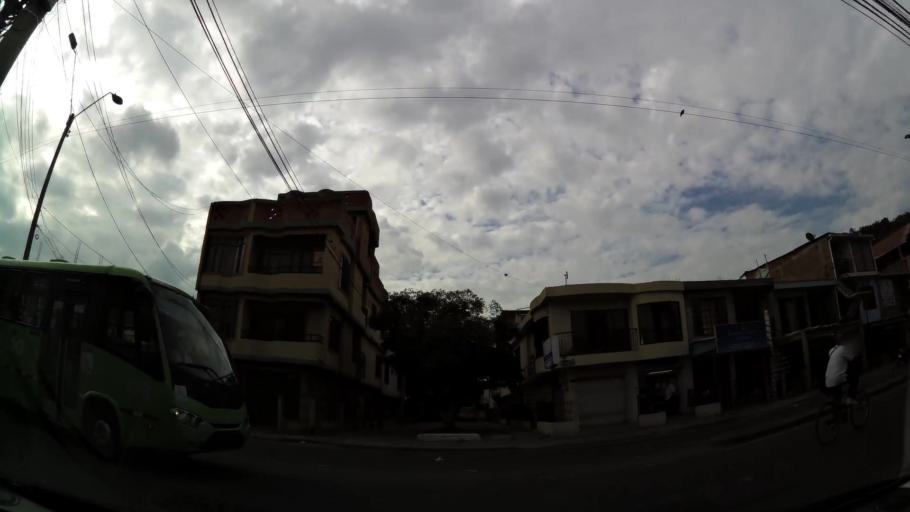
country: CO
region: Valle del Cauca
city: Cali
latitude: 3.4719
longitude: -76.4900
